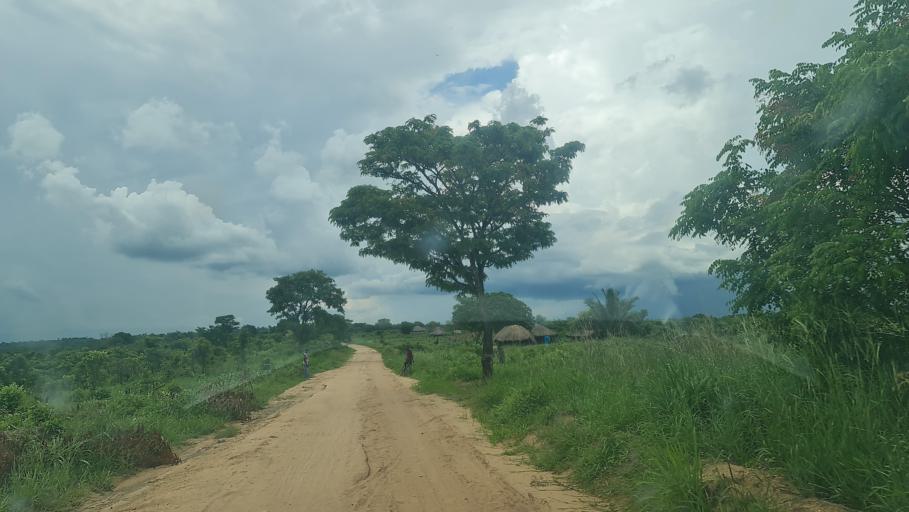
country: MW
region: Southern Region
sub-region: Nsanje District
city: Nsanje
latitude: -17.5792
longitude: 35.6613
